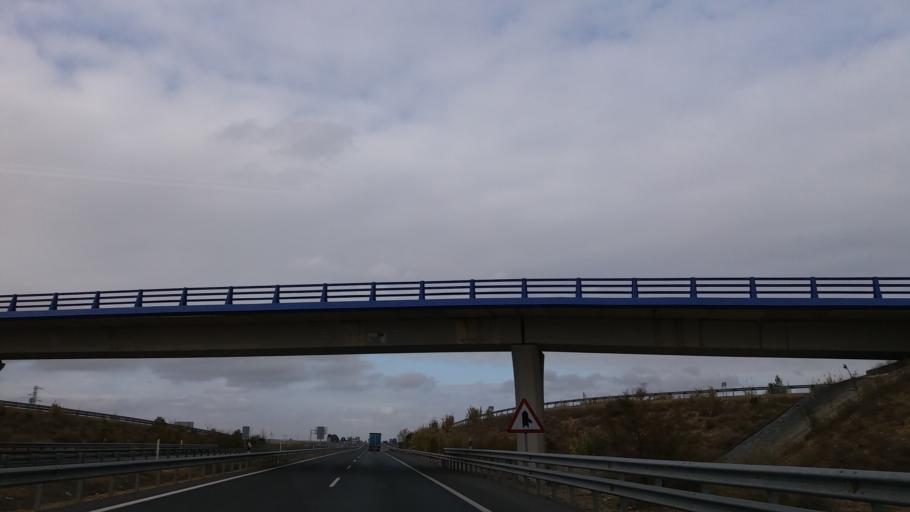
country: ES
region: Navarre
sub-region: Provincia de Navarra
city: Cortes
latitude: 41.9305
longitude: -1.4569
